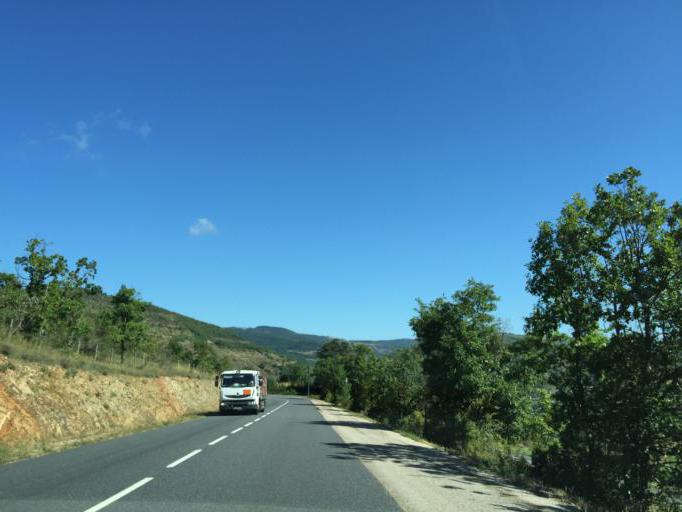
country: FR
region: Midi-Pyrenees
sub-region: Departement de l'Aveyron
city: Saint-Georges-de-Luzencon
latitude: 44.0647
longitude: 2.9110
